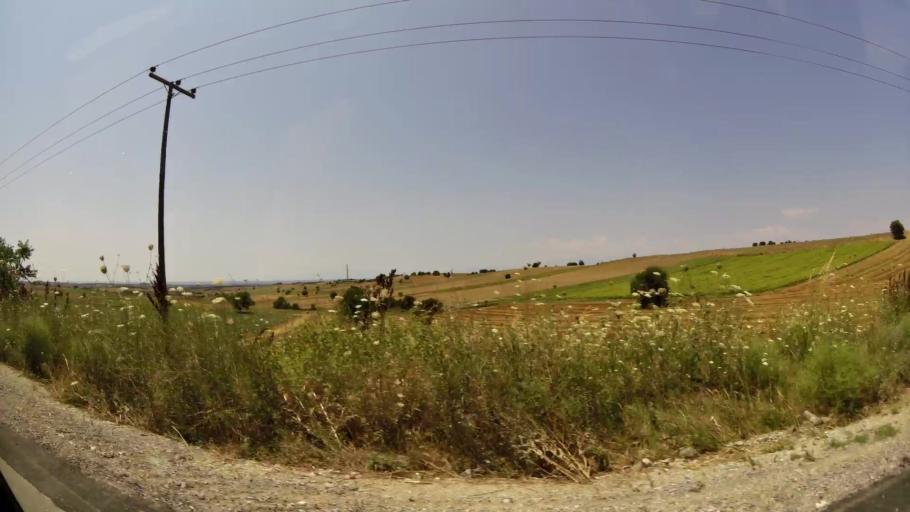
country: GR
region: Central Macedonia
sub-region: Nomos Thessalonikis
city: Neoi Epivates
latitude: 40.4648
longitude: 22.9043
